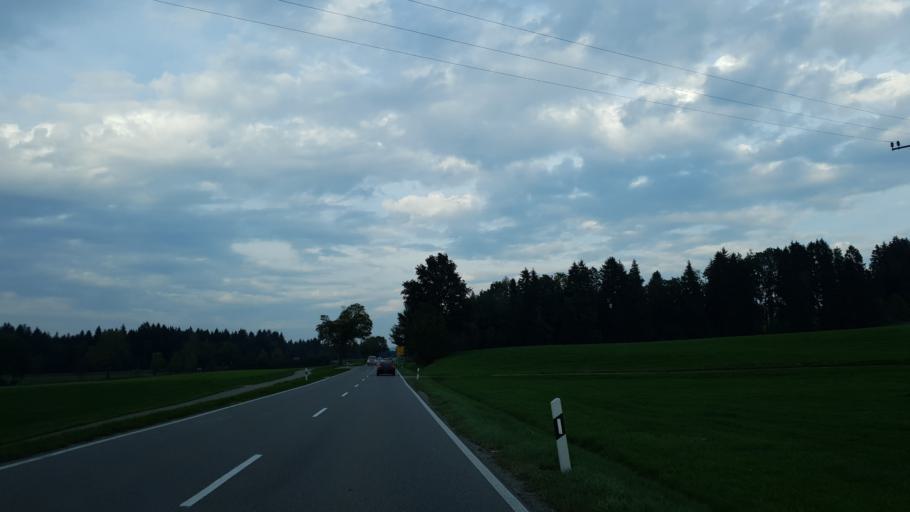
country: DE
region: Bavaria
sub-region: Swabia
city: Gestratz
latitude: 47.6761
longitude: 9.9669
